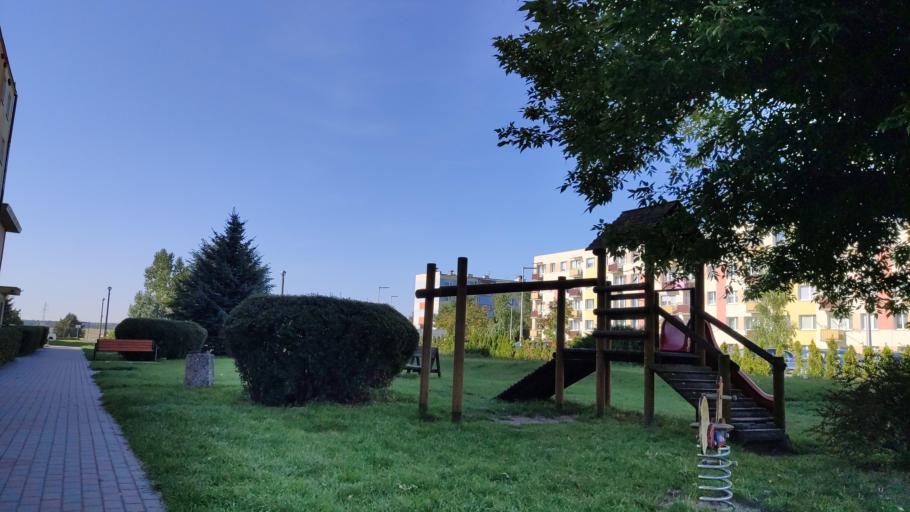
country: PL
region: Kujawsko-Pomorskie
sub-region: Powiat zninski
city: Barcin
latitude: 52.8537
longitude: 17.9485
